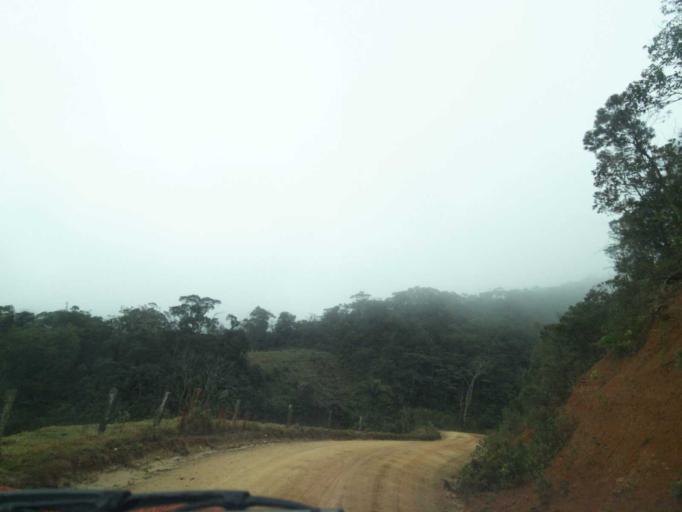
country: BR
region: Santa Catarina
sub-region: Anitapolis
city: Anitapolis
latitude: -27.9254
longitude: -49.1831
